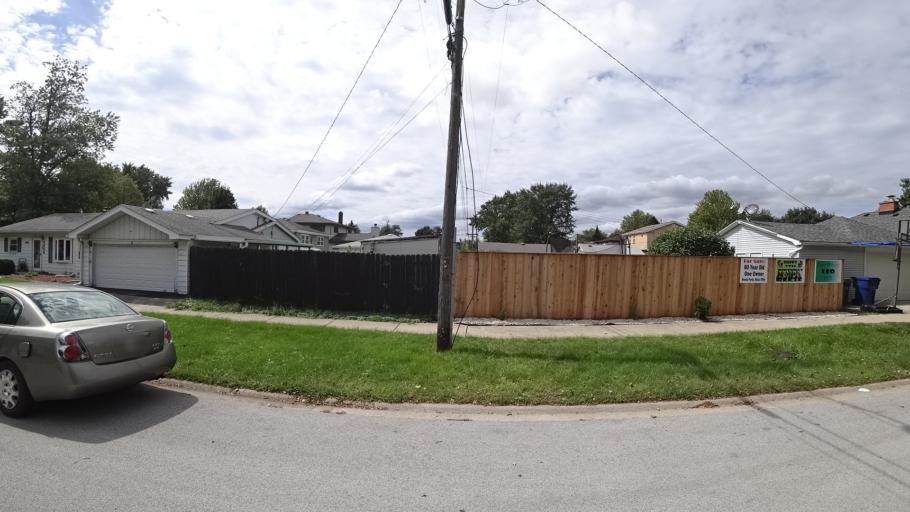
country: US
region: Illinois
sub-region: Cook County
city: Burbank
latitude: 41.7180
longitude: -87.7918
